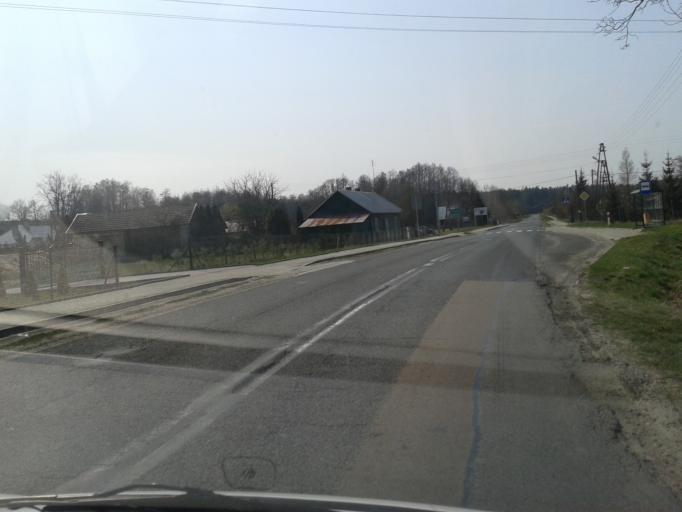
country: PL
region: Subcarpathian Voivodeship
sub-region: Powiat lubaczowski
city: Narol
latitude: 50.3123
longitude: 23.2427
